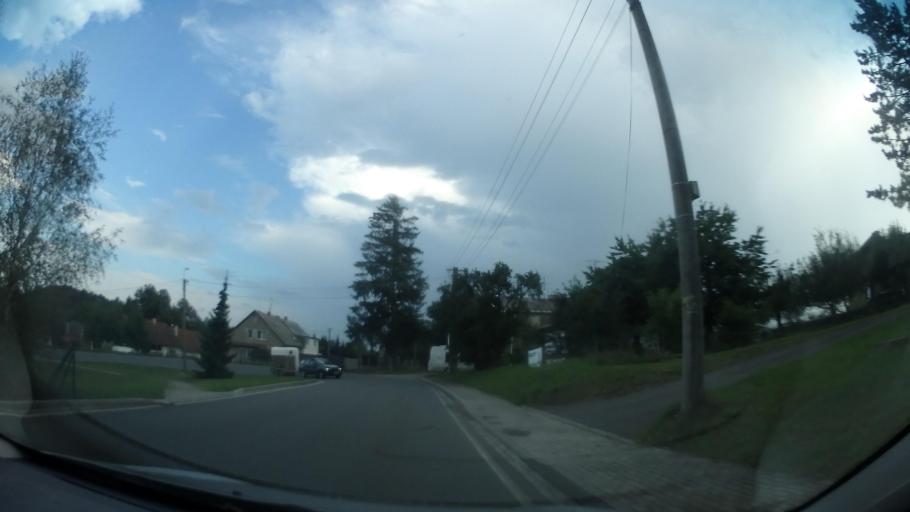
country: CZ
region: Olomoucky
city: Zabreh
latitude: 49.8817
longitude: 16.7982
